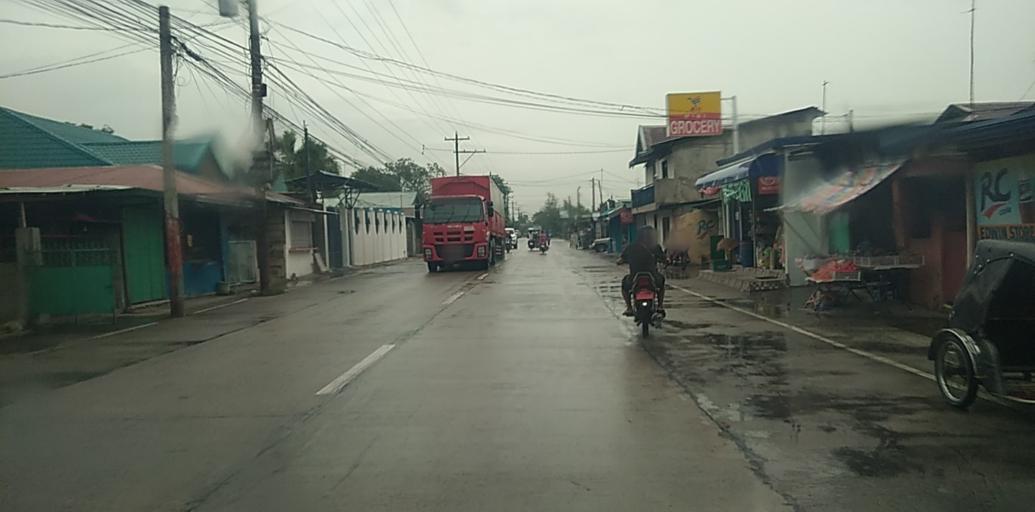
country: PH
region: Central Luzon
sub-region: Province of Pampanga
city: Anao
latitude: 15.1418
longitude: 120.6928
